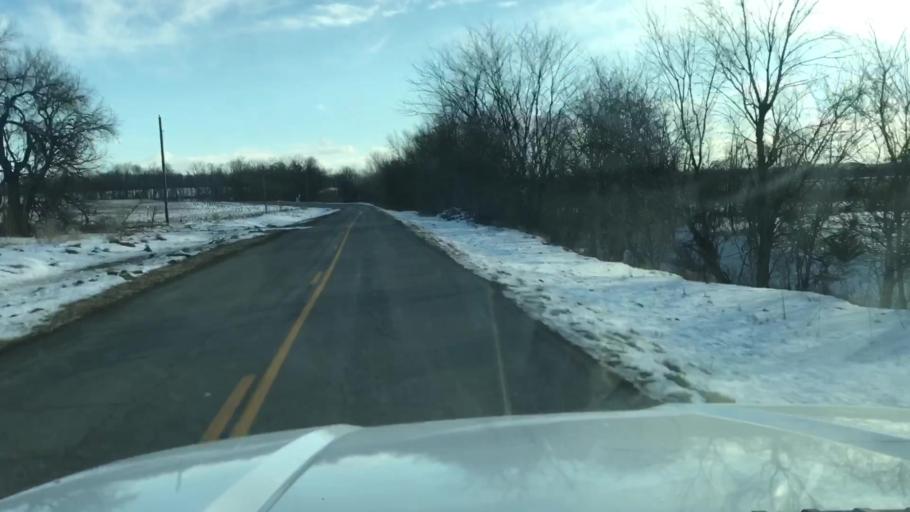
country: US
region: Missouri
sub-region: Holt County
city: Oregon
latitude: 40.1050
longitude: -95.0226
